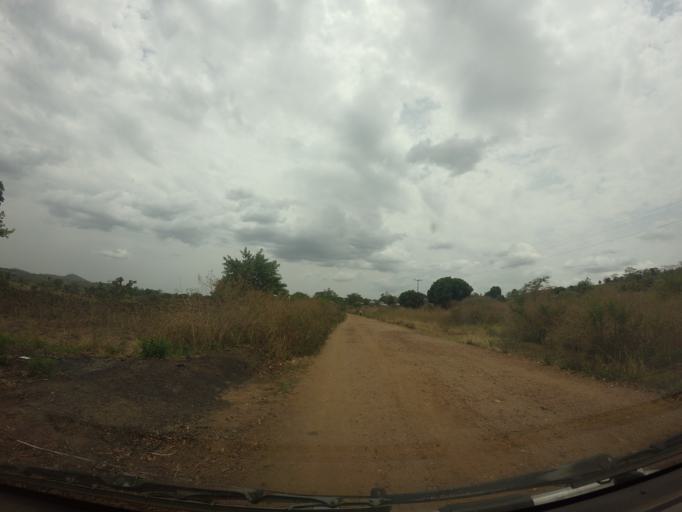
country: UG
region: Northern Region
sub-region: Arua District
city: Arua
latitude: 2.9481
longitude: 30.9393
